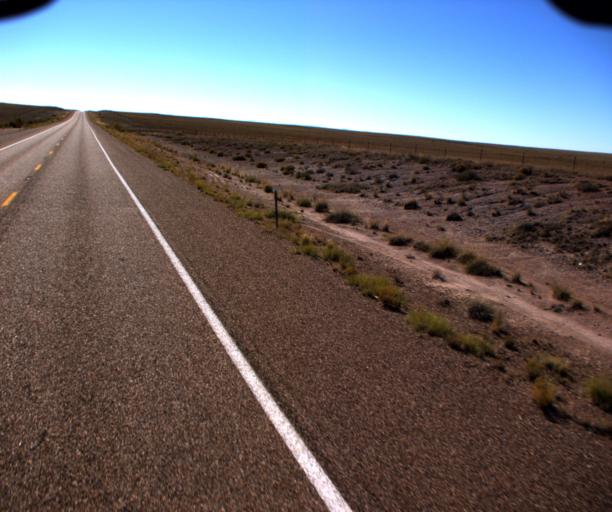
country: US
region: Arizona
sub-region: Navajo County
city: Holbrook
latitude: 34.8381
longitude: -109.9436
